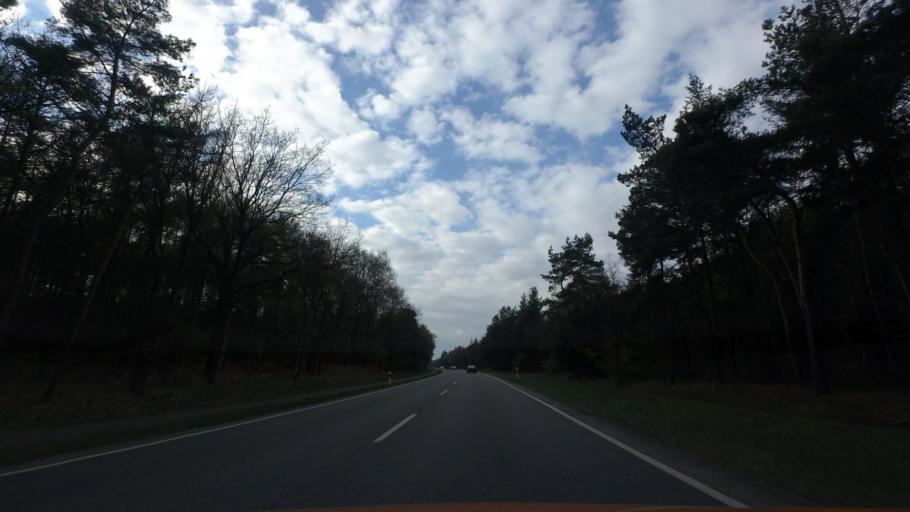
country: DE
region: Lower Saxony
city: Bosel
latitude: 52.9675
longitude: 7.9187
